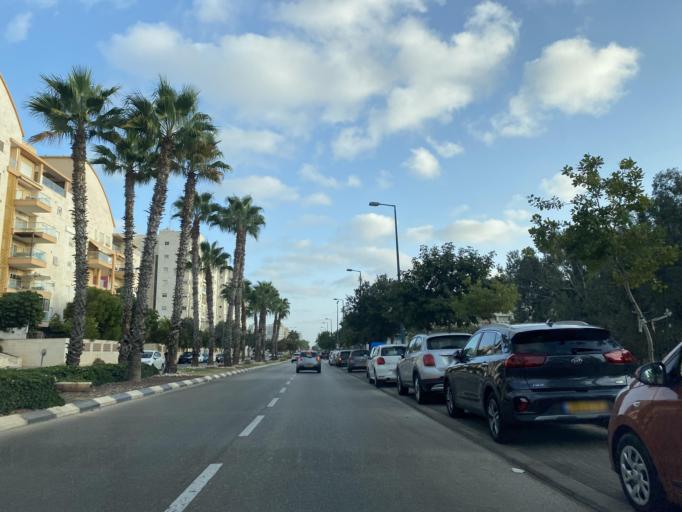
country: IL
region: Central District
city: Netanya
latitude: 32.3087
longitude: 34.8697
